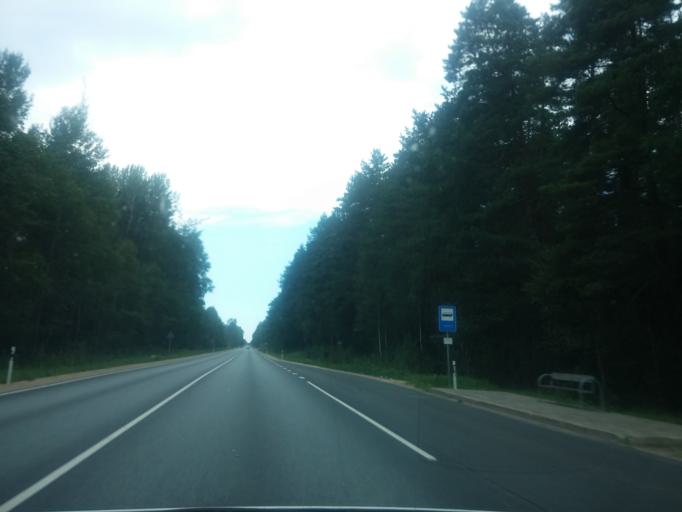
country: LV
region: Ikskile
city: Ikskile
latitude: 56.8765
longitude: 24.5256
